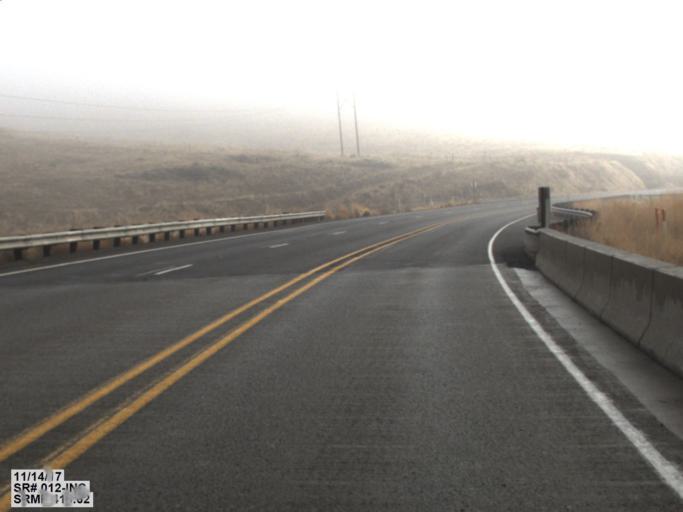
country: US
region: Washington
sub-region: Asotin County
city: Clarkston Heights-Vineland
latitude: 46.4367
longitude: -117.3253
